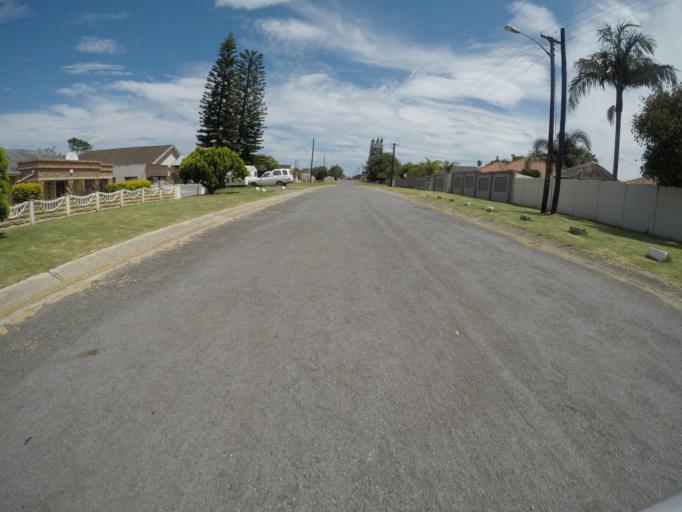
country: ZA
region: Eastern Cape
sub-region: Buffalo City Metropolitan Municipality
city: East London
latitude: -33.0313
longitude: 27.8663
